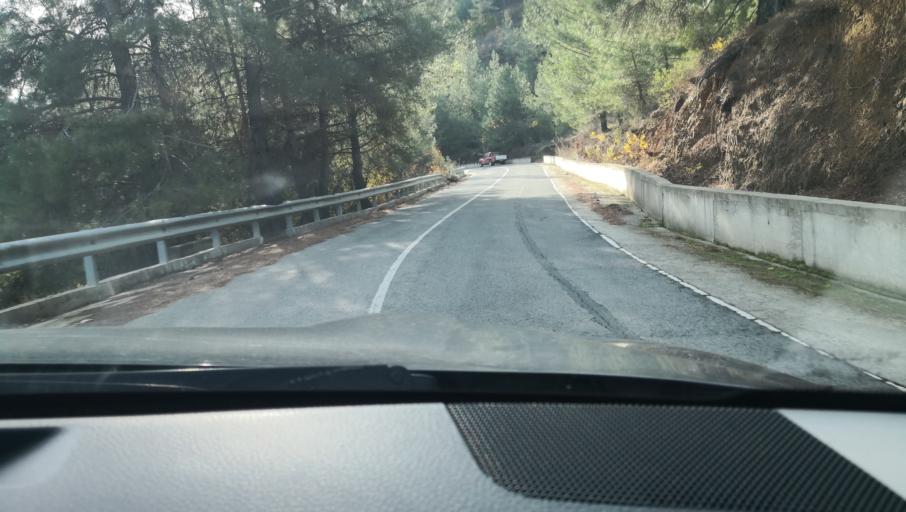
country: CY
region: Lefkosia
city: Lefka
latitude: 35.0190
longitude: 32.7260
